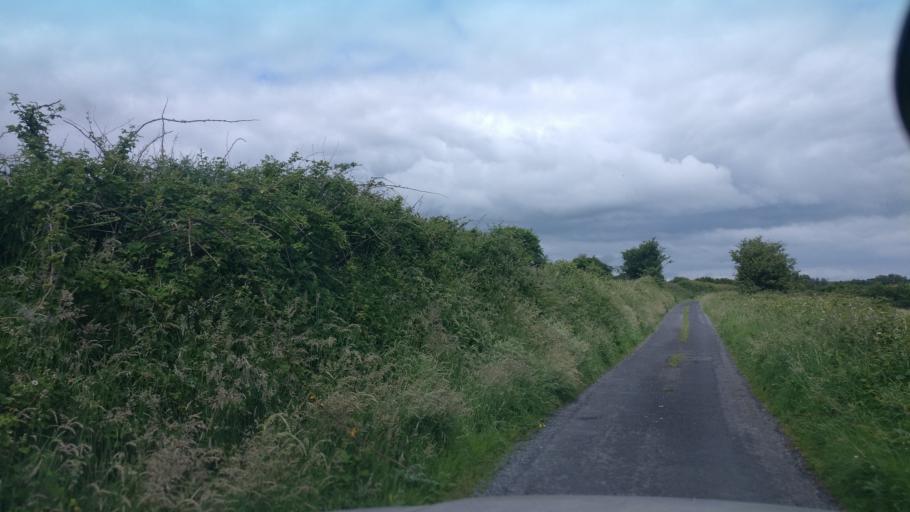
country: IE
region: Connaught
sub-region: County Galway
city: Loughrea
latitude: 53.1584
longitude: -8.5543
